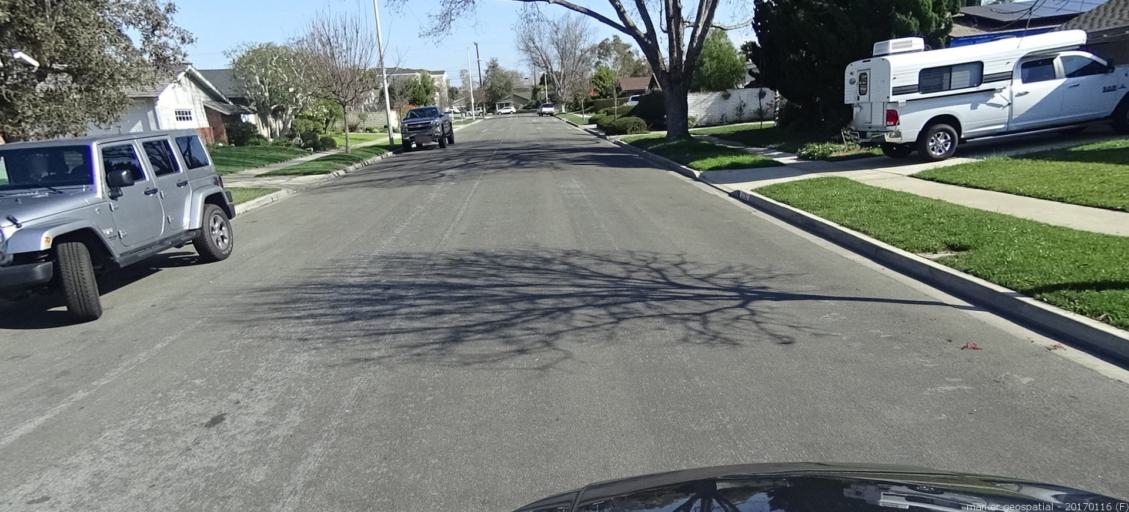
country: US
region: California
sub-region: Orange County
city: Rossmoor
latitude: 33.7772
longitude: -118.0854
